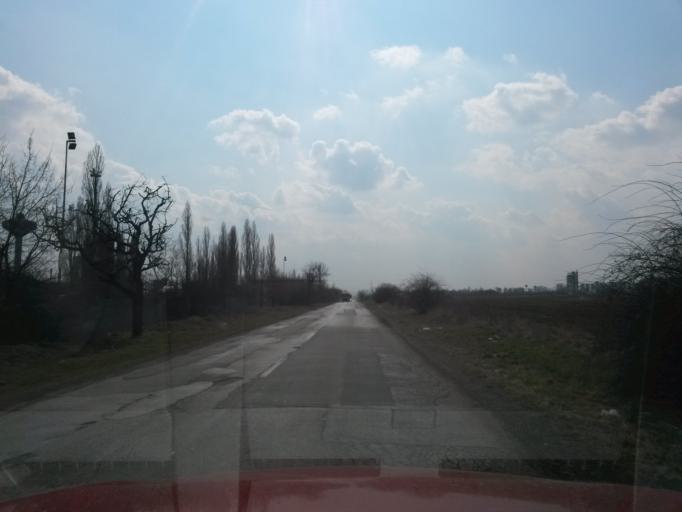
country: SK
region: Kosicky
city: Kosice
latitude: 48.6130
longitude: 21.1774
